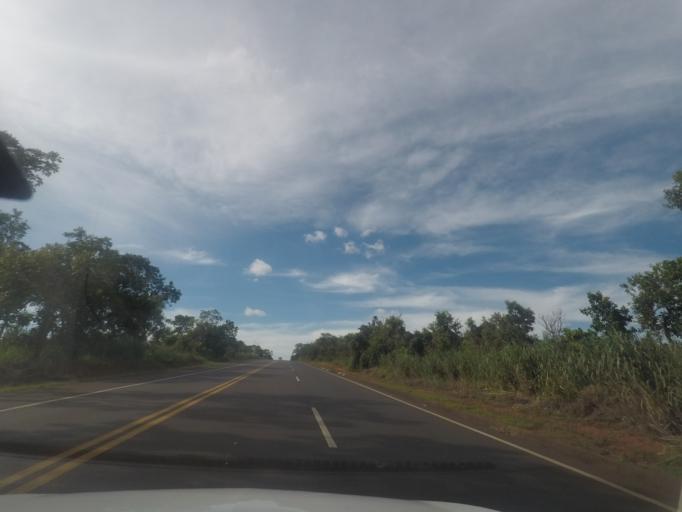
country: BR
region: Minas Gerais
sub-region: Monte Alegre De Minas
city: Monte Alegre de Minas
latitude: -18.9841
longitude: -49.0225
